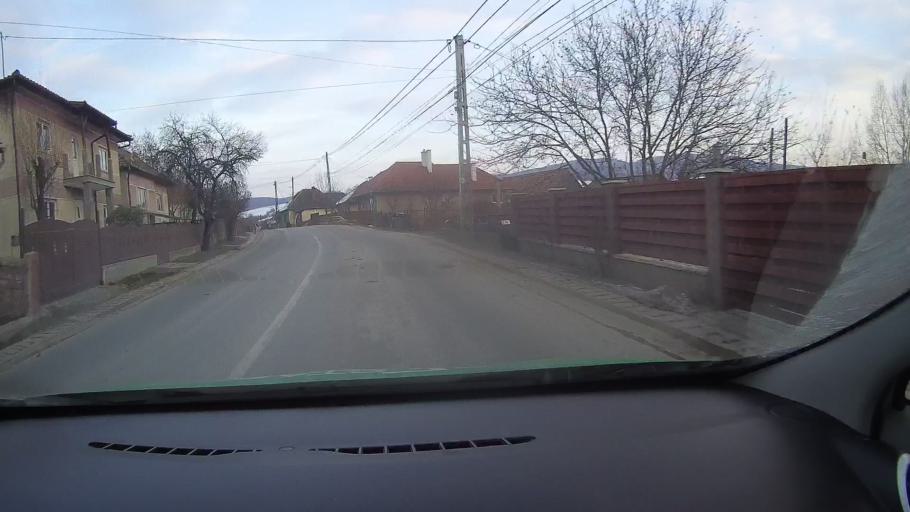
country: RO
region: Harghita
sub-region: Comuna Simonesti
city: Simonesti
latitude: 46.3572
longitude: 25.1509
